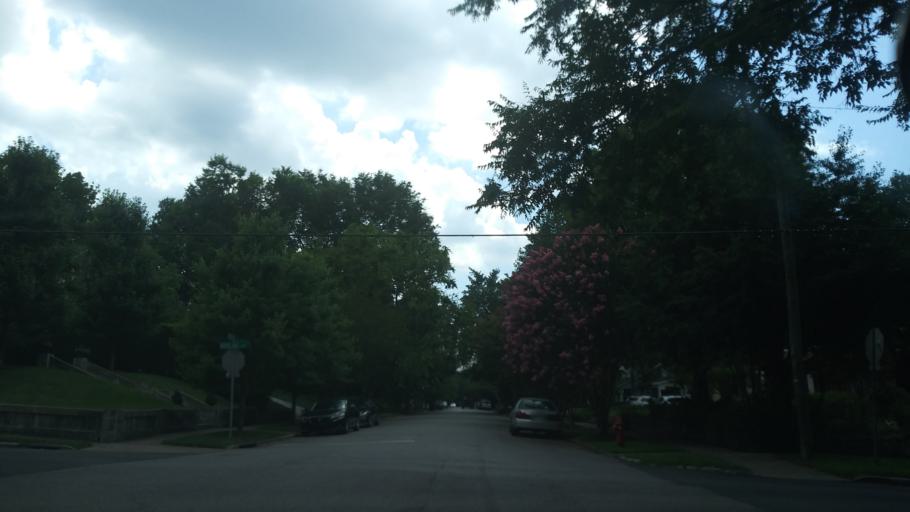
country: US
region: Tennessee
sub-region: Davidson County
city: Nashville
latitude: 36.1371
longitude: -86.8263
